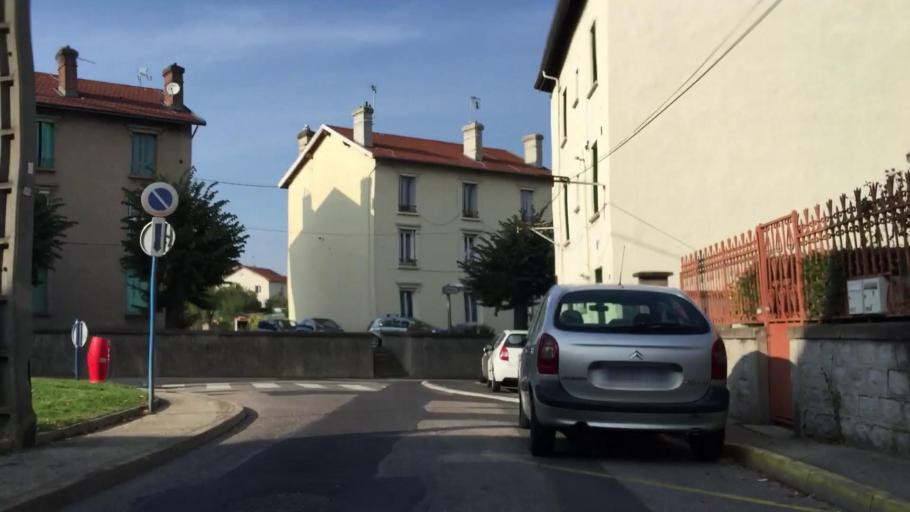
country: FR
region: Rhone-Alpes
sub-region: Departement de la Loire
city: Saint-Chamond
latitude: 45.4591
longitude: 4.5033
